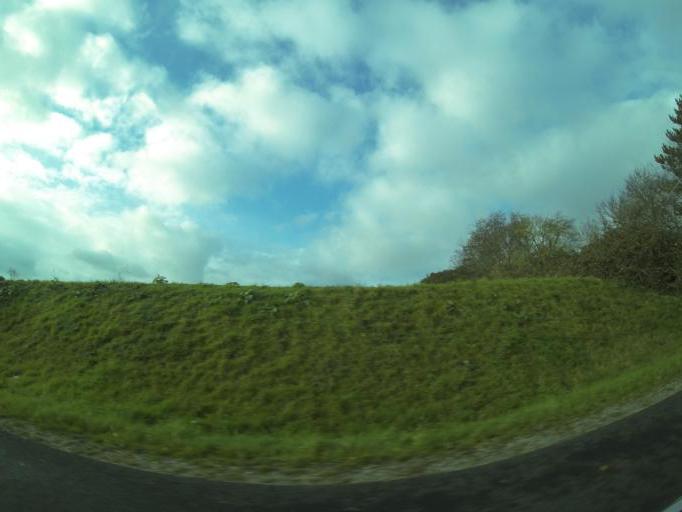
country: DE
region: Thuringia
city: Saara
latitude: 50.9565
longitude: 12.4290
